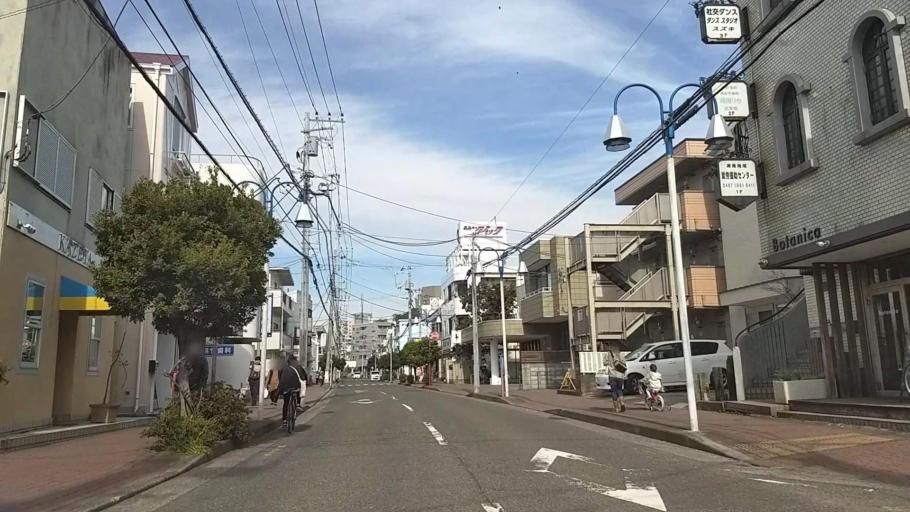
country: JP
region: Kanagawa
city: Fujisawa
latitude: 35.3348
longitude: 139.4404
